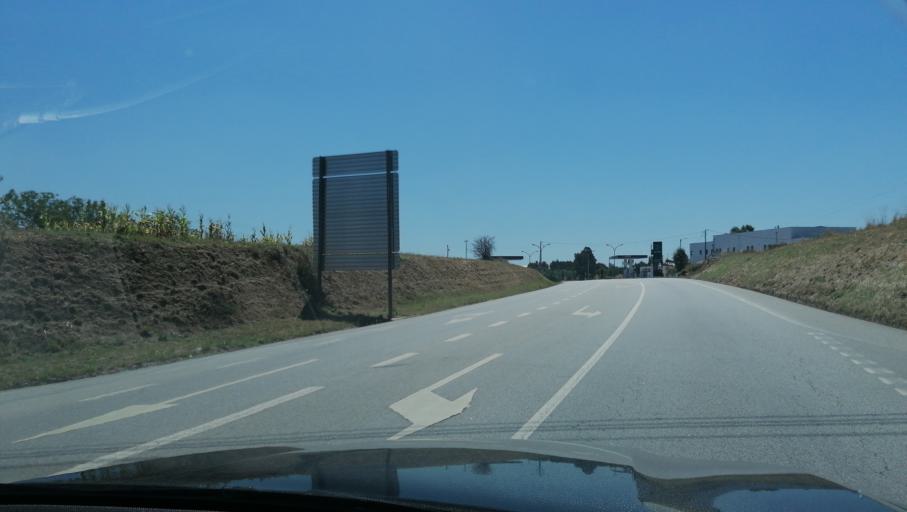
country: PT
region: Aveiro
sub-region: Agueda
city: Aguada de Cima
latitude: 40.5118
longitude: -8.4500
